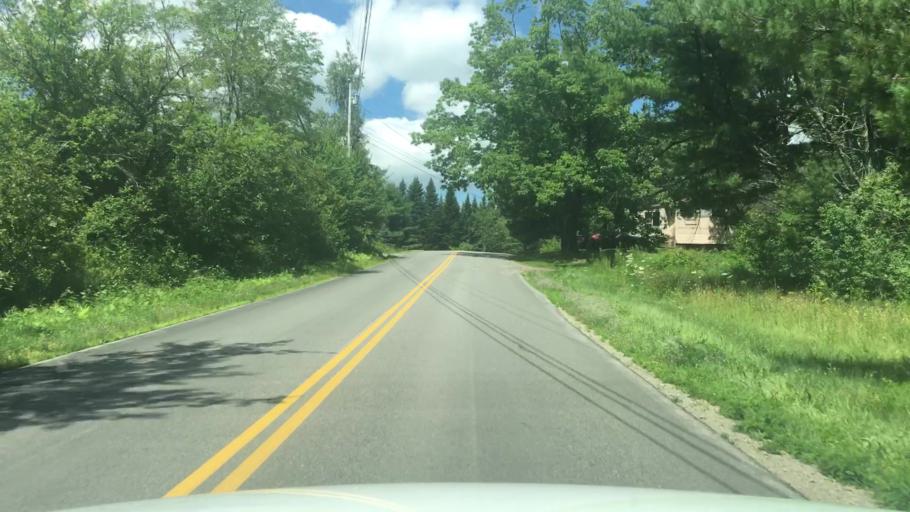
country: US
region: Maine
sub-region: Waldo County
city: Belfast
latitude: 44.4074
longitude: -69.0333
